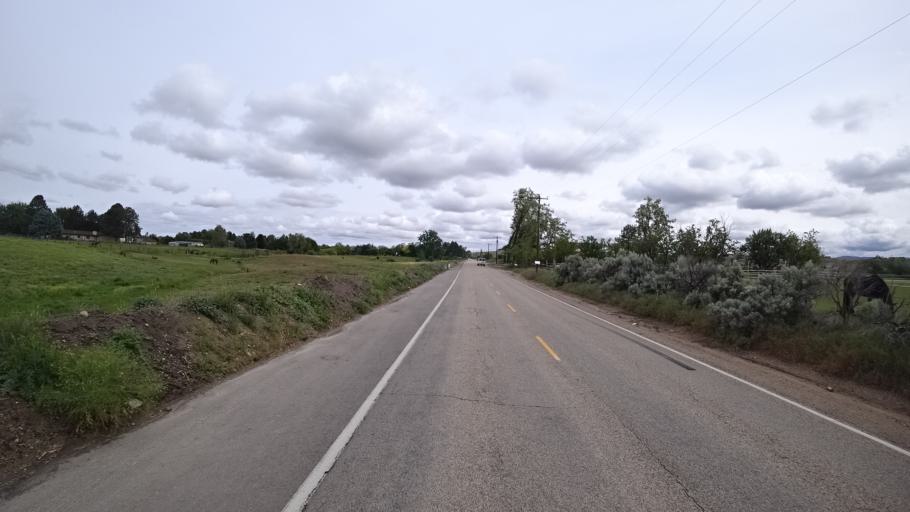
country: US
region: Idaho
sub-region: Ada County
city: Eagle
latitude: 43.7239
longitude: -116.3543
